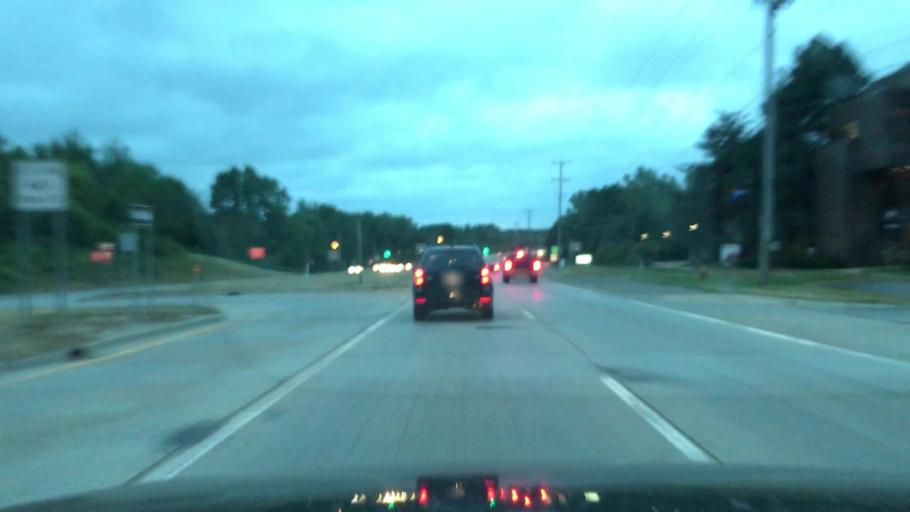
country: US
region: Michigan
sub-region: Kent County
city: East Grand Rapids
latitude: 42.9354
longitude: -85.5849
